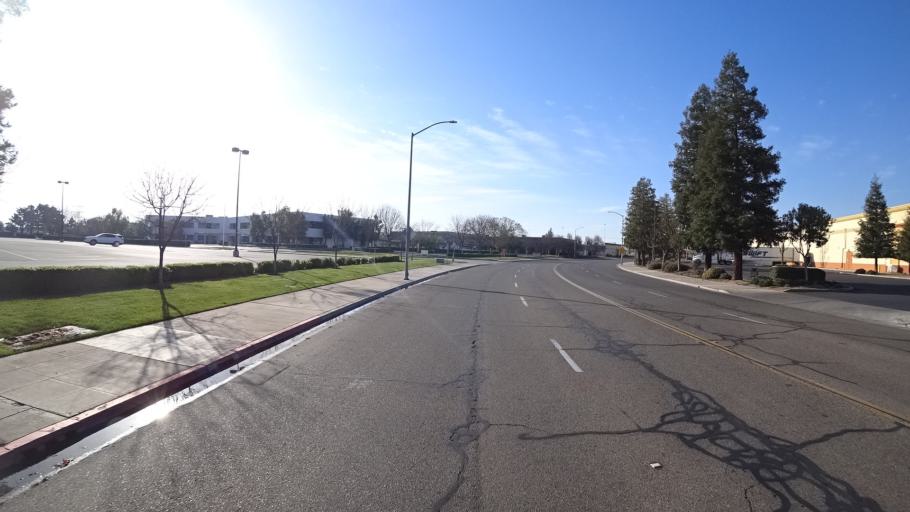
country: US
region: California
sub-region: Fresno County
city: West Park
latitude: 36.8110
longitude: -119.8712
